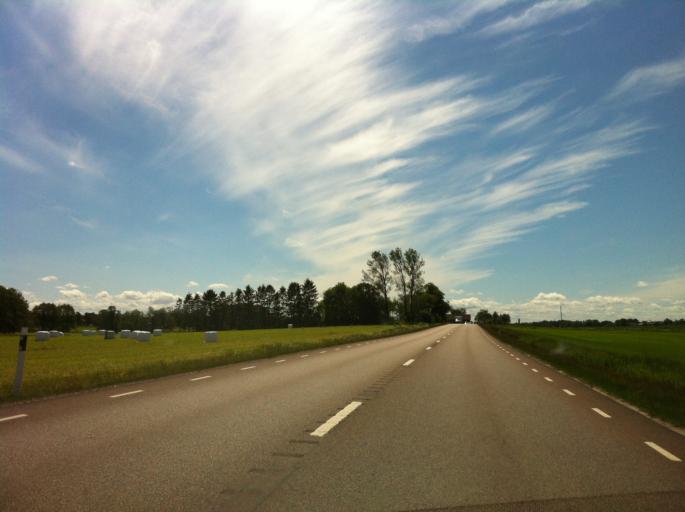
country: SE
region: Vaestra Goetaland
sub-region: Vanersborgs Kommun
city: Bralanda
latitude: 58.5272
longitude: 12.3145
